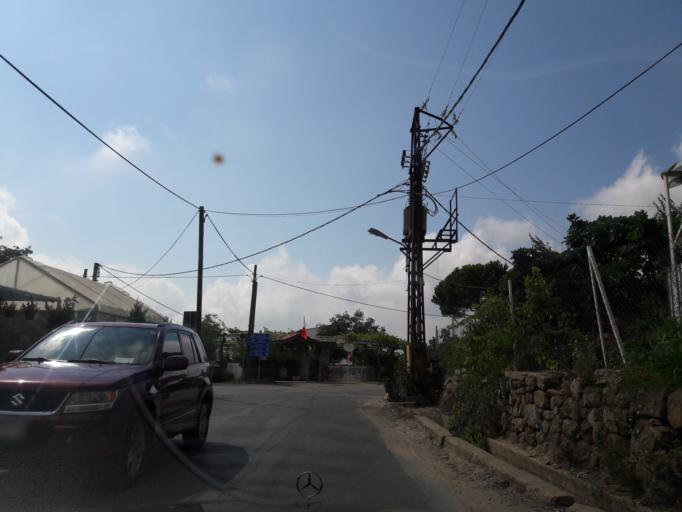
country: LB
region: Mont-Liban
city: Djounie
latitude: 33.9551
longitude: 35.7761
